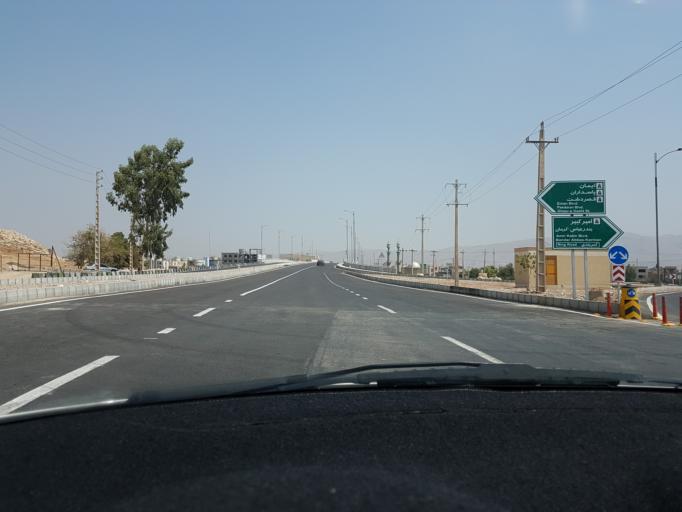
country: IR
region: Fars
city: Shiraz
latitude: 29.6296
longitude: 52.4551
